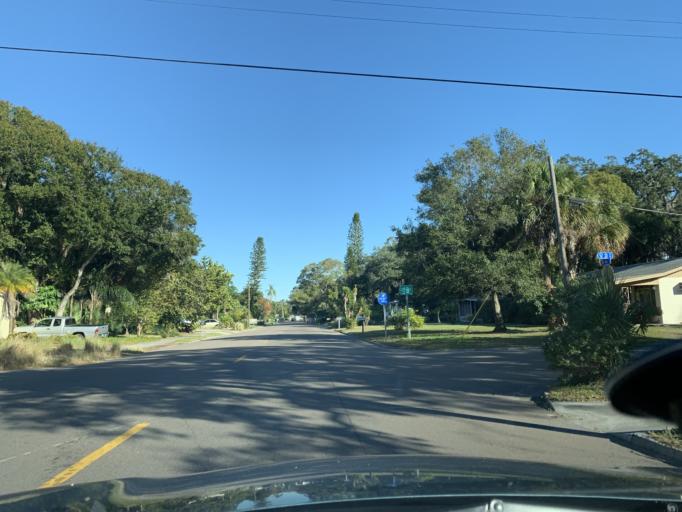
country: US
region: Florida
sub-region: Pinellas County
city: Gulfport
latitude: 27.7422
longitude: -82.7040
